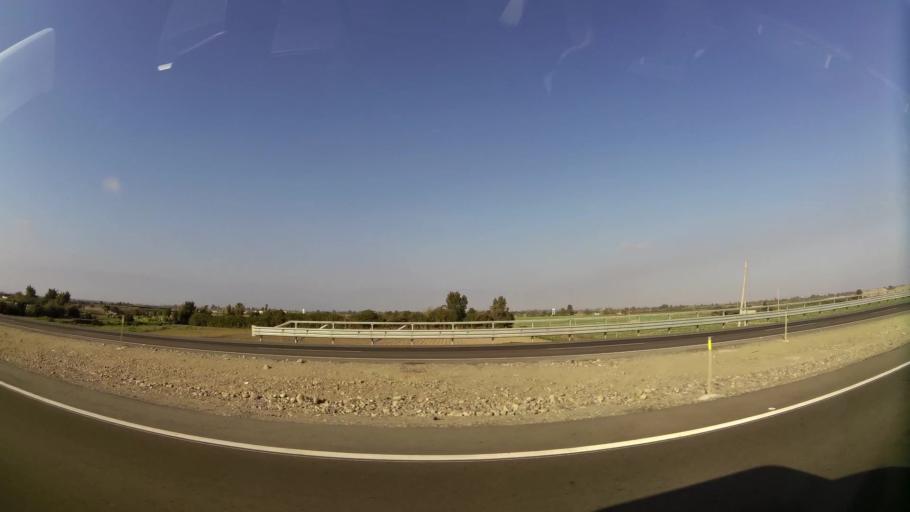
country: PE
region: Ica
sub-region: Provincia de Chincha
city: Chincha Baja
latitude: -13.5206
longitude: -76.1833
